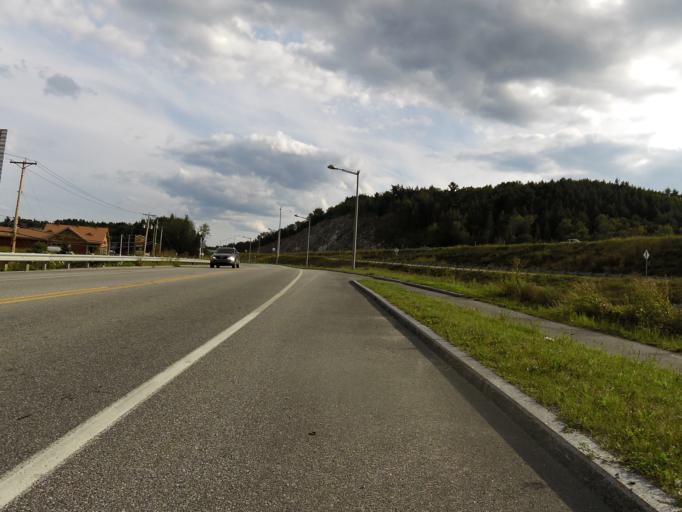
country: CA
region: Quebec
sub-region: Outaouais
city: Wakefield
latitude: 45.6260
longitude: -75.9352
